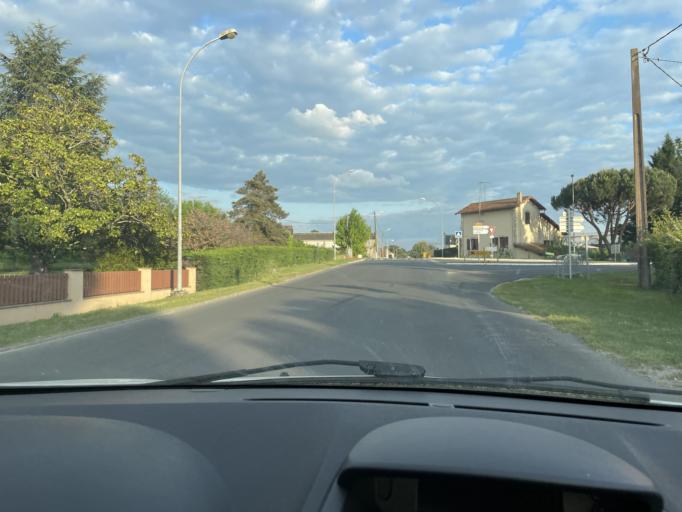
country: FR
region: Aquitaine
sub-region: Departement du Lot-et-Garonne
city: Casteljaloux
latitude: 44.3188
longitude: 0.0792
